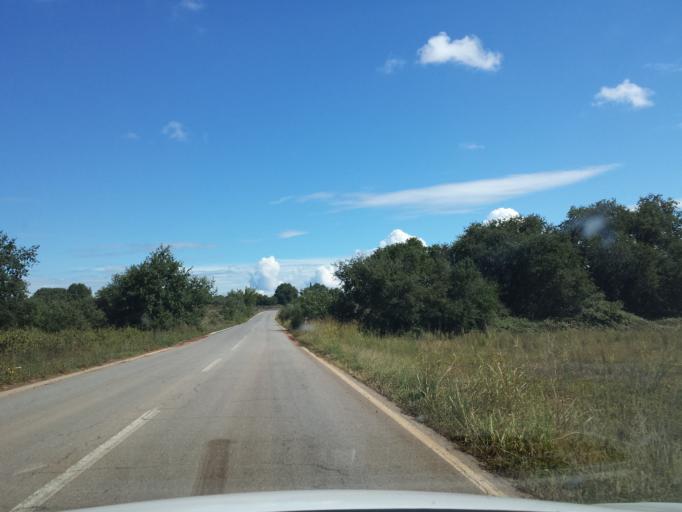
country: GR
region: Peloponnese
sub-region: Nomos Messinias
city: Vlakhopoulon
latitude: 36.9780
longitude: 21.8164
